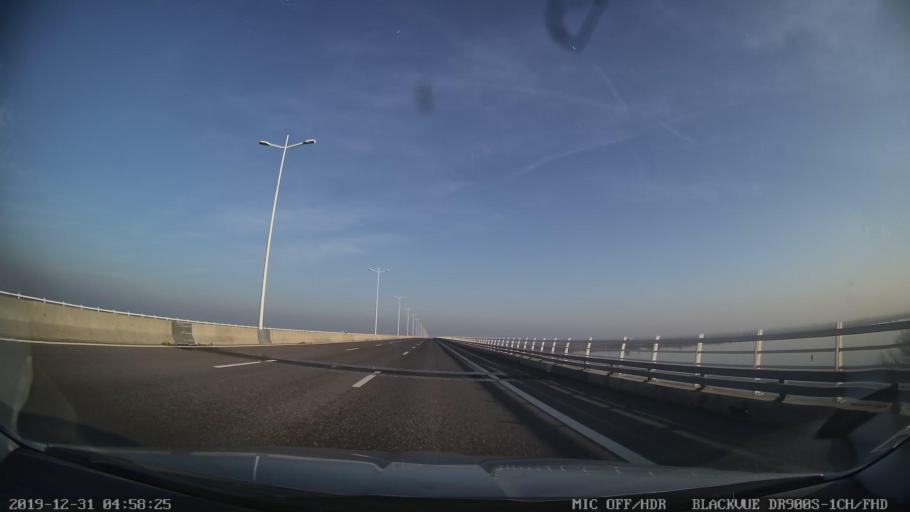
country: PT
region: Lisbon
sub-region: Alenquer
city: Carregado
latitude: 39.0130
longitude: -8.9382
